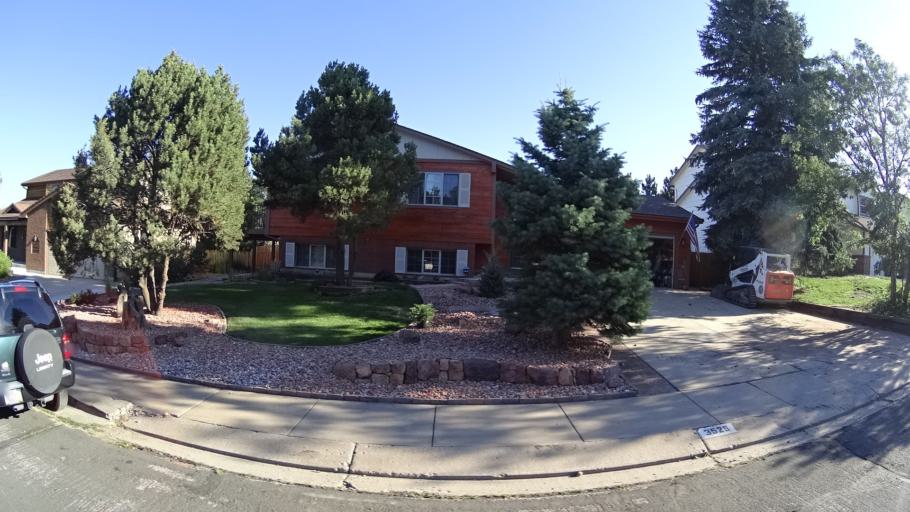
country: US
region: Colorado
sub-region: El Paso County
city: Black Forest
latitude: 38.9562
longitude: -104.7685
